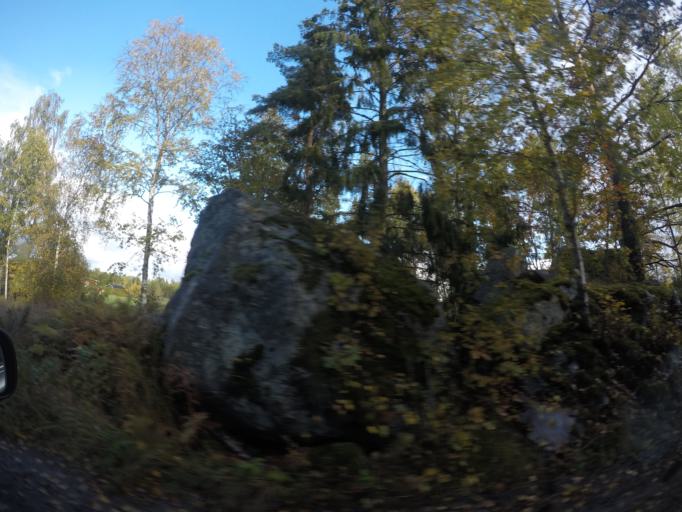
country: SE
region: Soedermanland
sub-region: Eskilstuna Kommun
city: Kvicksund
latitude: 59.3513
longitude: 16.3287
